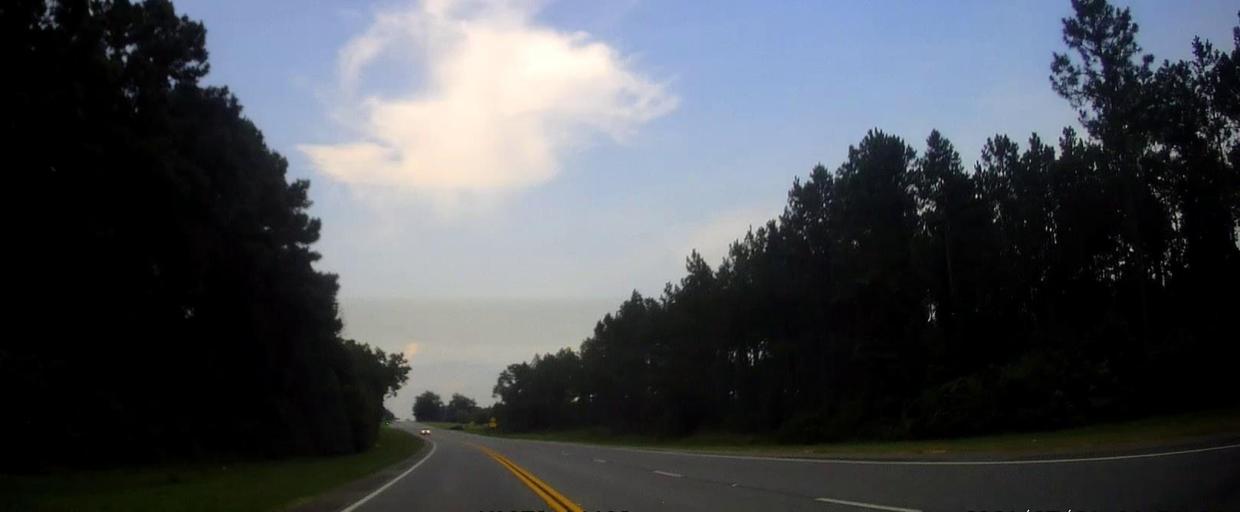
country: US
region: Georgia
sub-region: Laurens County
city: East Dublin
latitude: 32.6149
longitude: -82.8157
